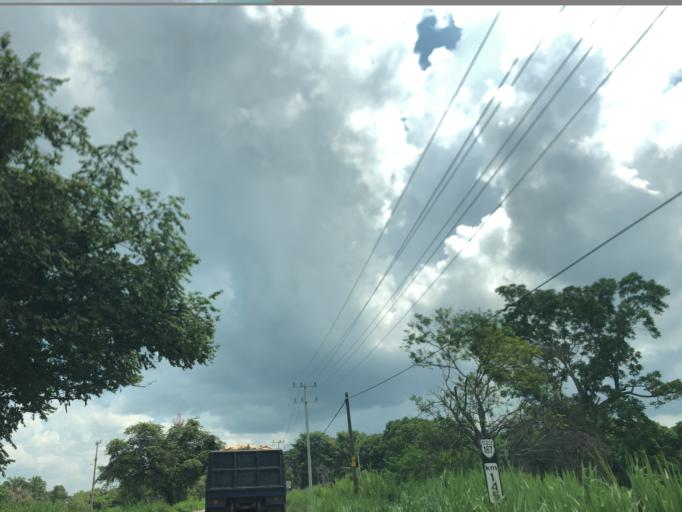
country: MX
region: Tabasco
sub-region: Comalcalco
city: Oriente 6ta. Seccion (Los Mulatos)
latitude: 18.1720
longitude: -93.2412
